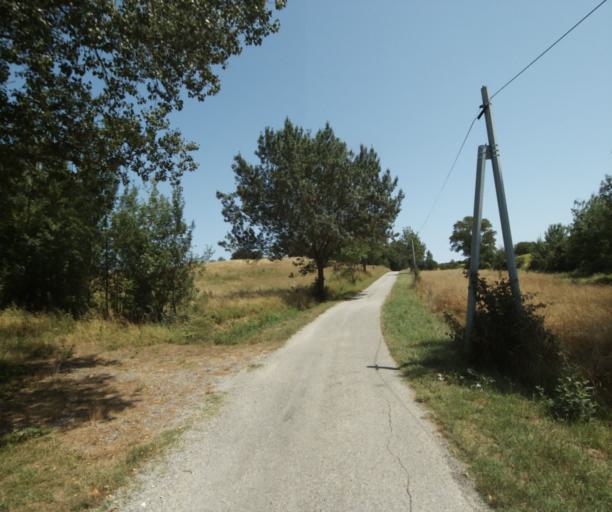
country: FR
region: Midi-Pyrenees
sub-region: Departement de la Haute-Garonne
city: Saint-Felix-Lauragais
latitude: 43.4561
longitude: 1.8423
